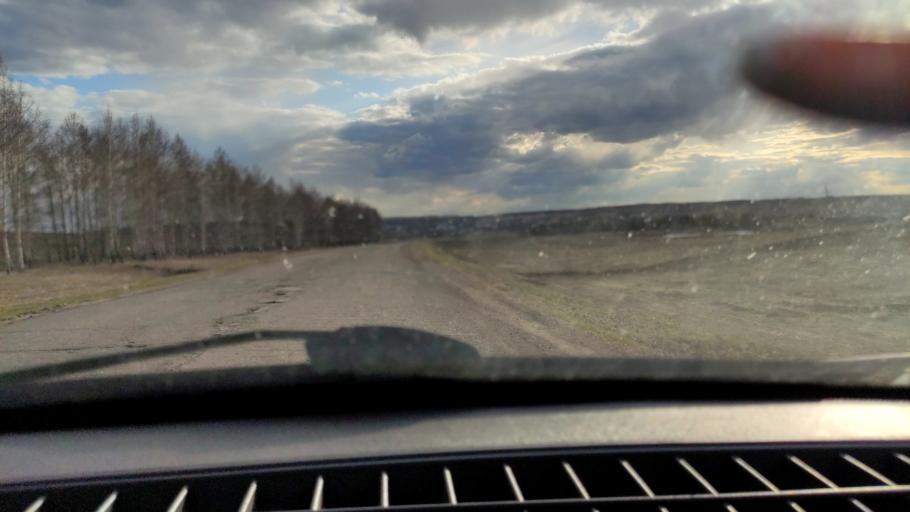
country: RU
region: Bashkortostan
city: Karmaskaly
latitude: 54.3422
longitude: 56.0181
